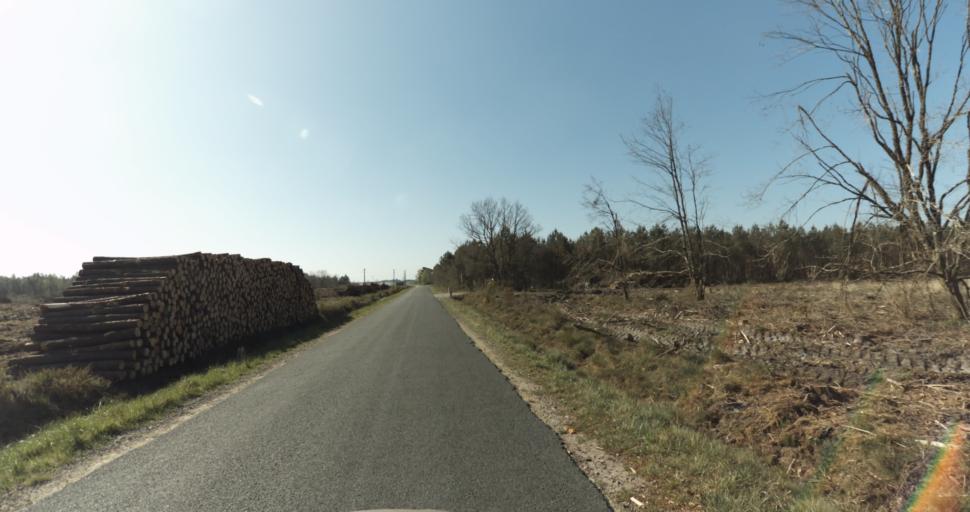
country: FR
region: Aquitaine
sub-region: Departement de la Gironde
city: Marcheprime
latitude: 44.7777
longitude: -0.8596
